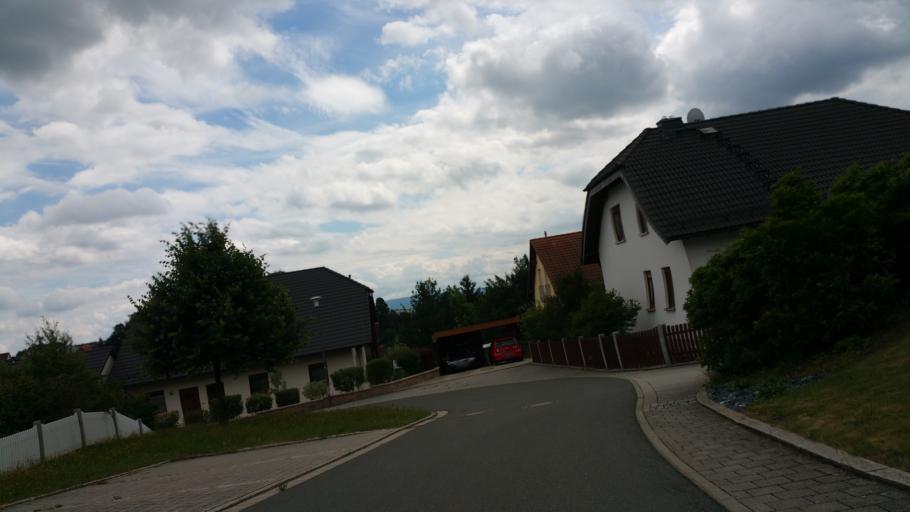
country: DE
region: Bavaria
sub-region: Upper Franconia
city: Oberkotzau
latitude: 50.2665
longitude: 11.9380
